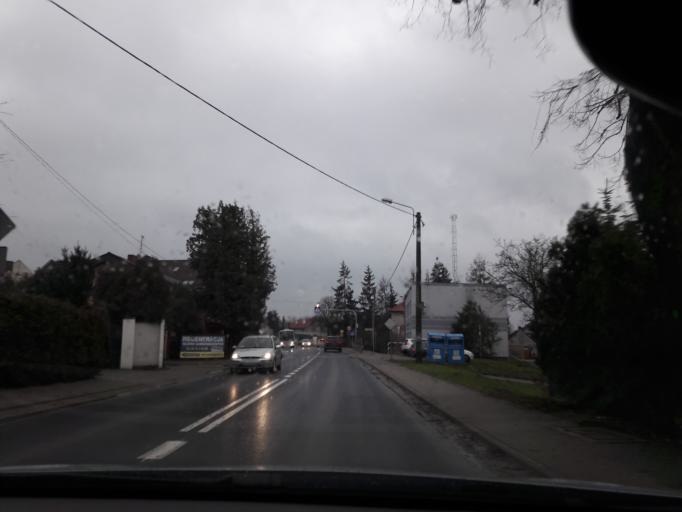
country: PL
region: Greater Poland Voivodeship
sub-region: Powiat poznanski
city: Suchy Las
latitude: 52.4759
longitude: 16.8789
